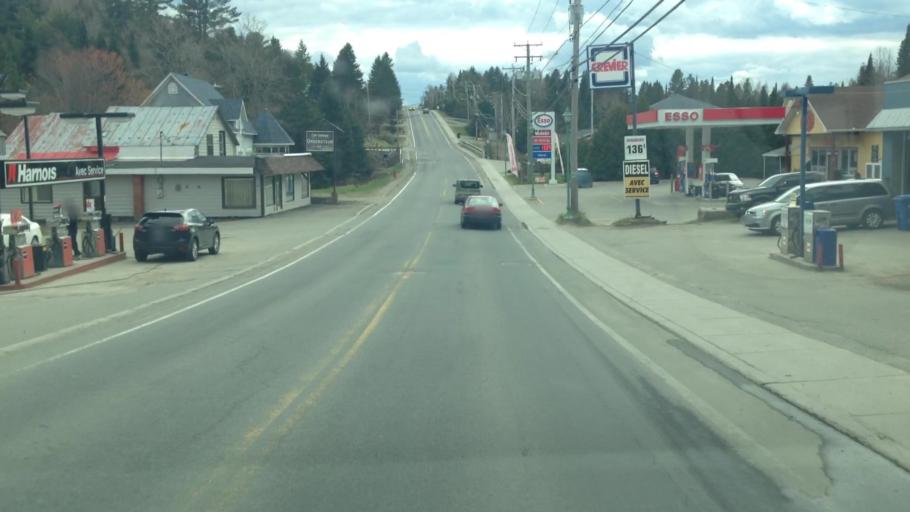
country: CA
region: Quebec
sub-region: Laurentides
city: Sainte-Adele
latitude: 46.0288
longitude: -74.0622
